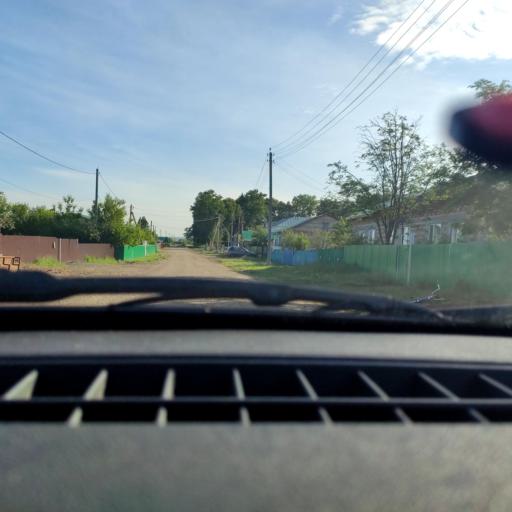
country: RU
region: Bashkortostan
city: Tolbazy
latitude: 54.2978
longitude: 55.8112
